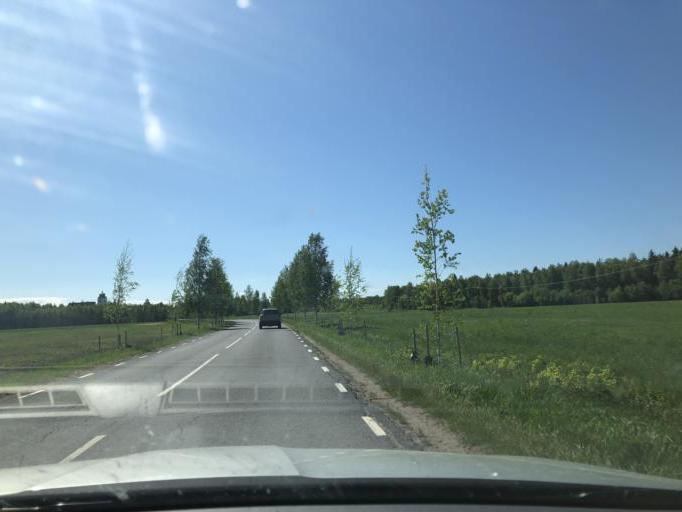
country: SE
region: Norrbotten
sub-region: Lulea Kommun
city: Gammelstad
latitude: 65.6529
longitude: 22.0169
